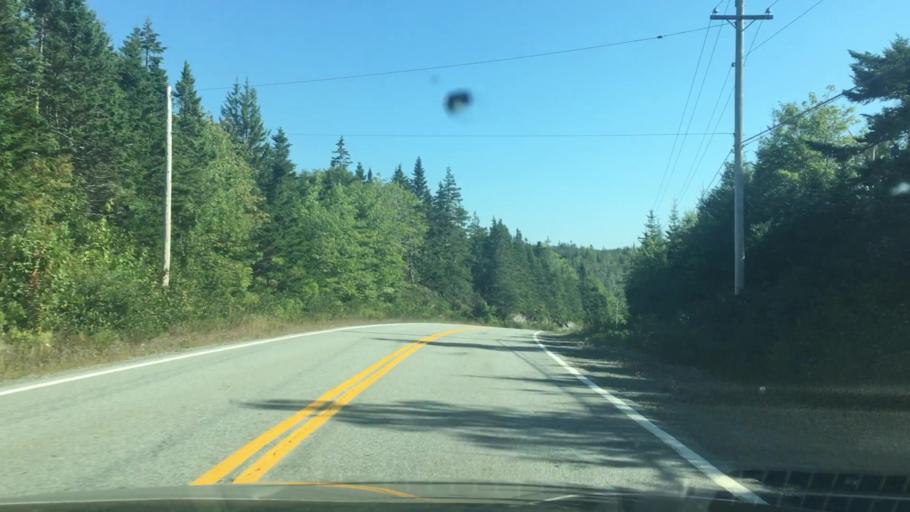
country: CA
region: Nova Scotia
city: Cole Harbour
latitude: 44.8041
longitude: -62.7099
